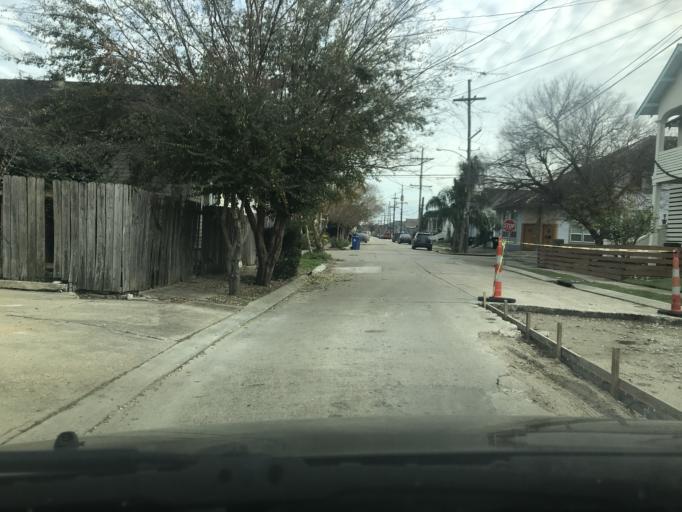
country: US
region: Louisiana
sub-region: Orleans Parish
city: New Orleans
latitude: 29.9534
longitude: -90.1063
